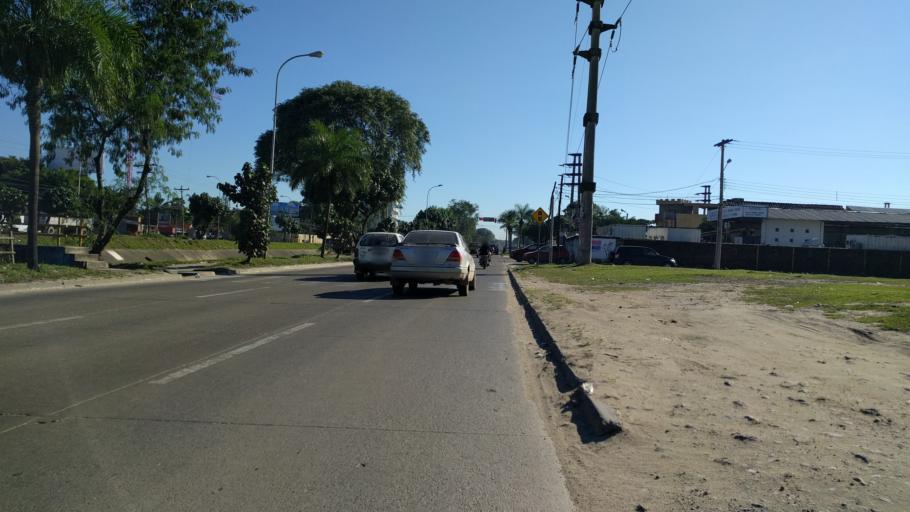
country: BO
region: Santa Cruz
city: Santa Cruz de la Sierra
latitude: -17.7875
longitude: -63.2165
